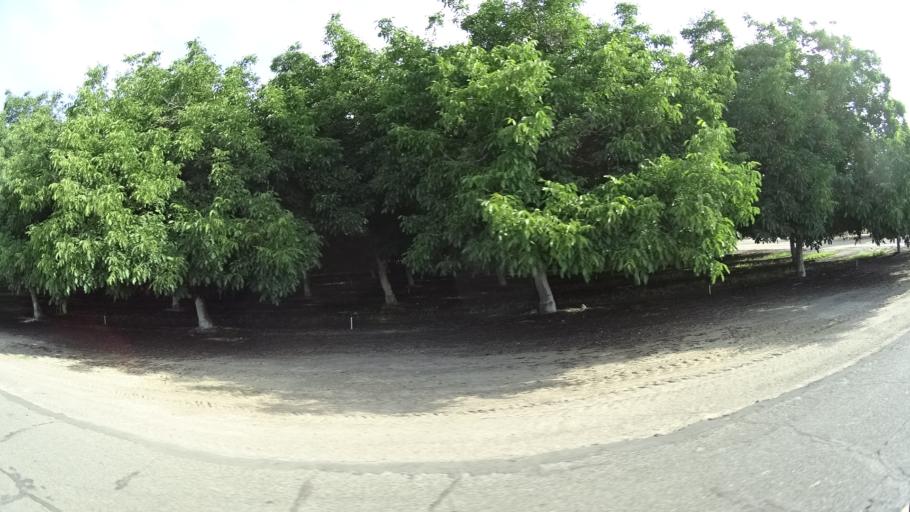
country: US
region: California
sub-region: Fresno County
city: Kingsburg
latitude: 36.4160
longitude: -119.5472
